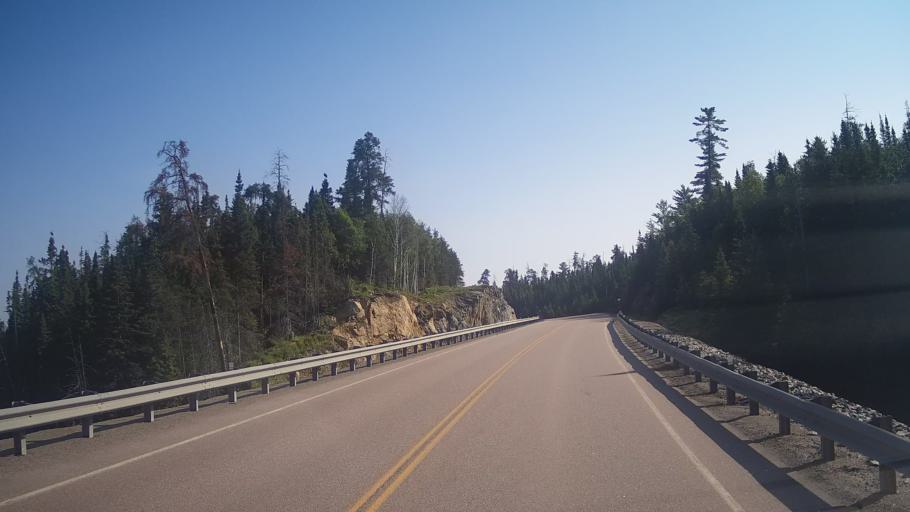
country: CA
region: Ontario
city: Rayside-Balfour
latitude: 47.0259
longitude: -81.6388
